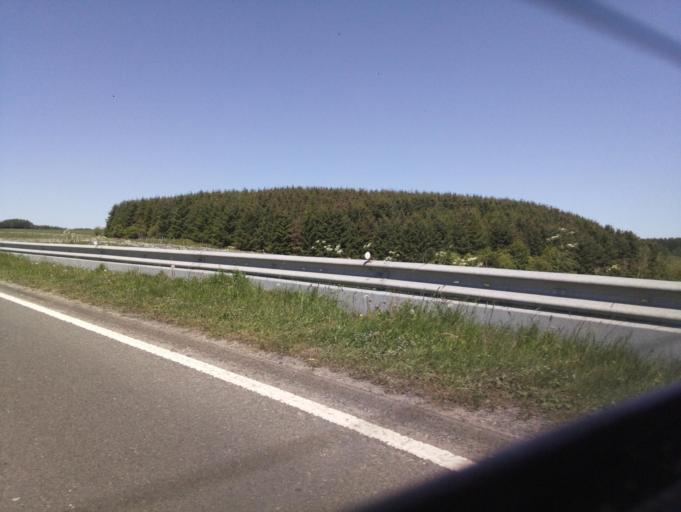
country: GB
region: Scotland
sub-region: The Scottish Borders
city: Hawick
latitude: 55.4610
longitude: -2.7804
